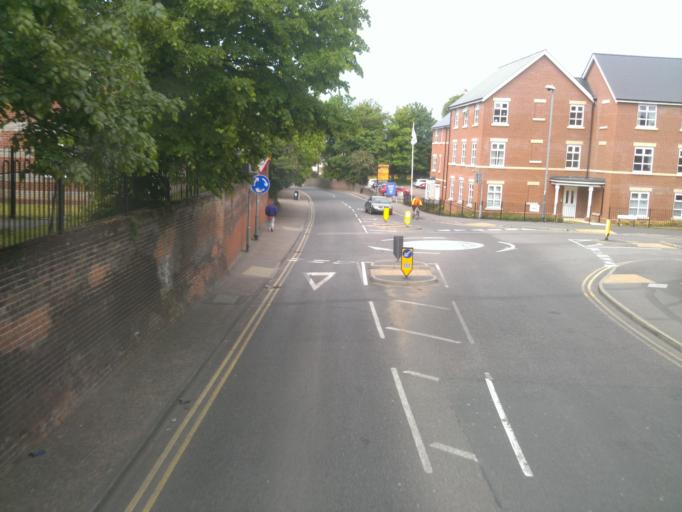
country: GB
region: England
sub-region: Essex
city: Colchester
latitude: 51.8859
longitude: 0.9137
